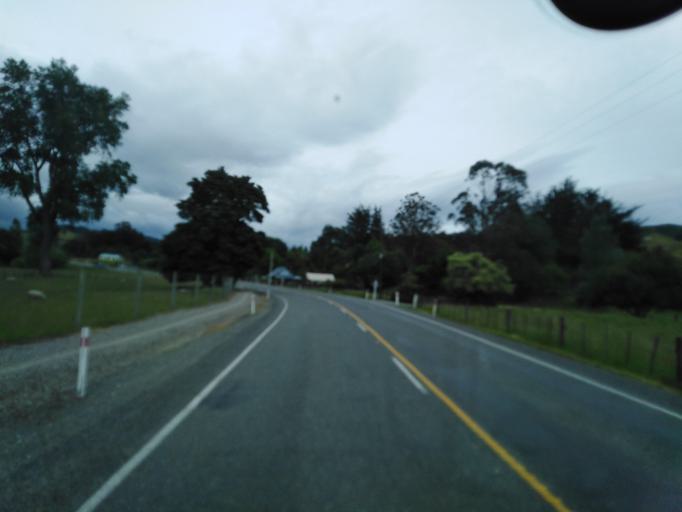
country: NZ
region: Tasman
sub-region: Tasman District
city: Wakefield
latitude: -41.4554
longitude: 172.9552
